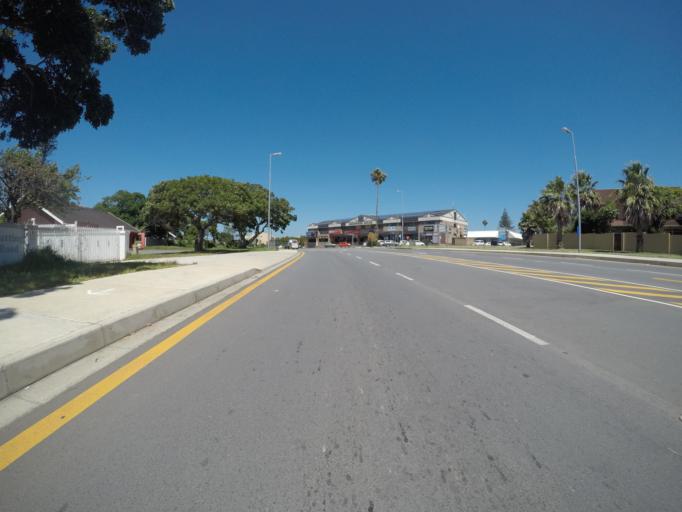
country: ZA
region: Eastern Cape
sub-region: Buffalo City Metropolitan Municipality
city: East London
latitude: -32.9637
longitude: 27.9341
